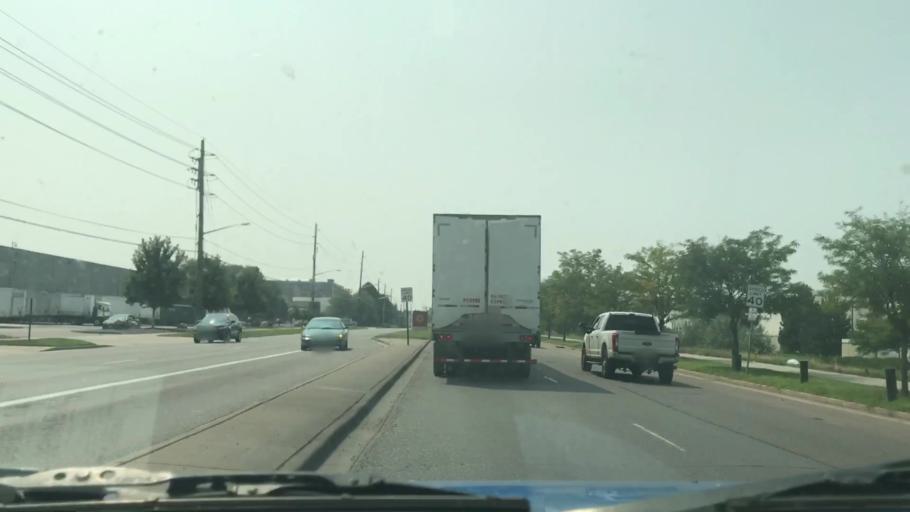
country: US
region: Colorado
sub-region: Adams County
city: Aurora
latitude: 39.7827
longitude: -104.8659
